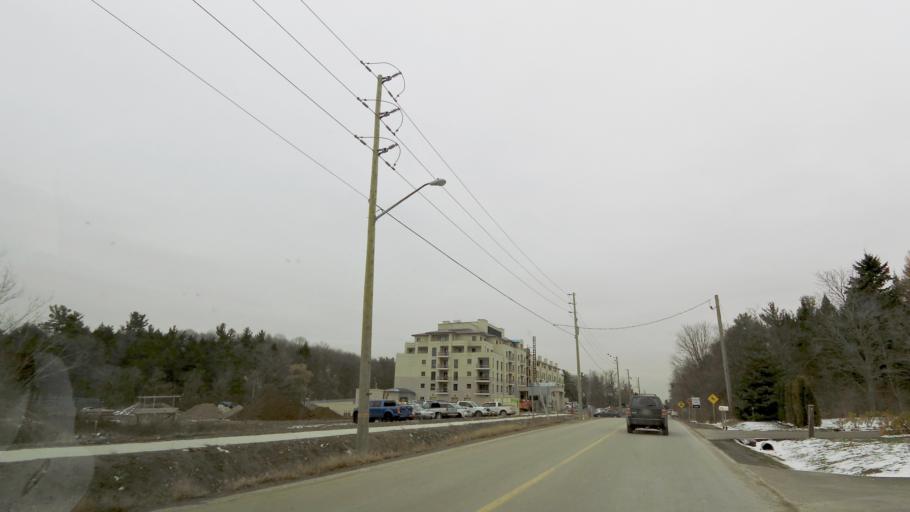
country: CA
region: Ontario
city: Vaughan
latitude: 43.8391
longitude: -79.5862
